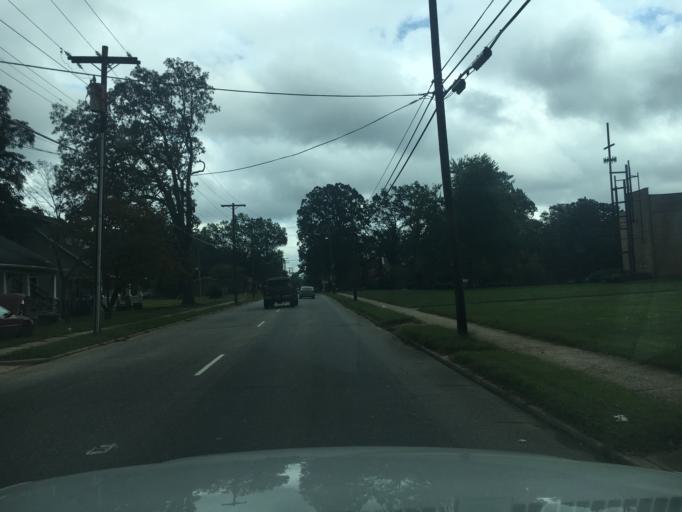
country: US
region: North Carolina
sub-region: Catawba County
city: Hickory
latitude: 35.7295
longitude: -81.3325
